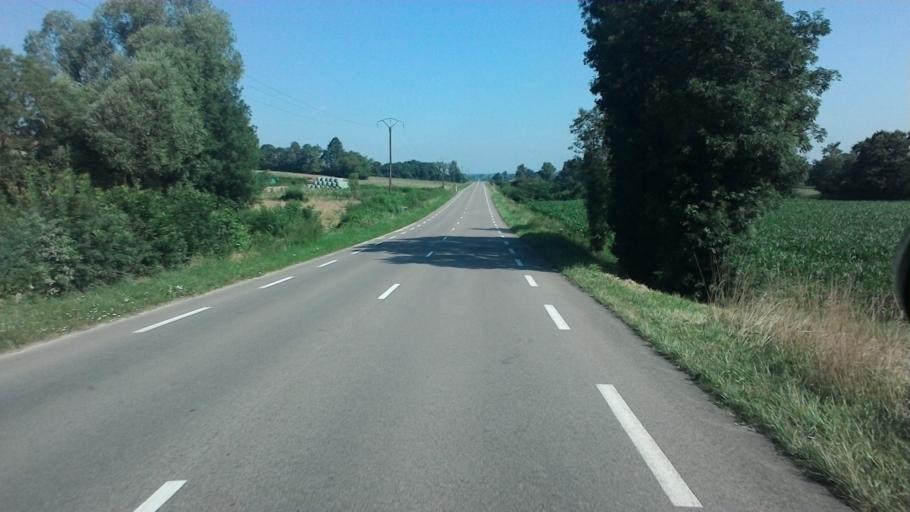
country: FR
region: Rhone-Alpes
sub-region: Departement de l'Ain
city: Montrevel-en-Bresse
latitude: 46.3747
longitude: 5.1193
